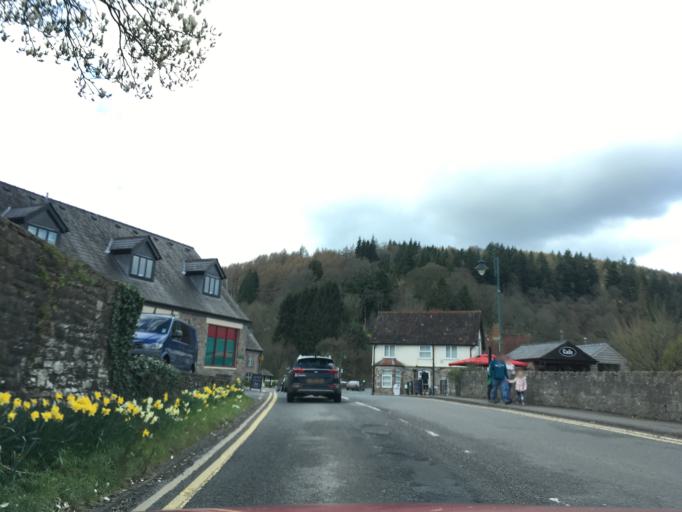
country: GB
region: Wales
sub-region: Monmouthshire
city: Tintern
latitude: 51.6979
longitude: -2.6808
